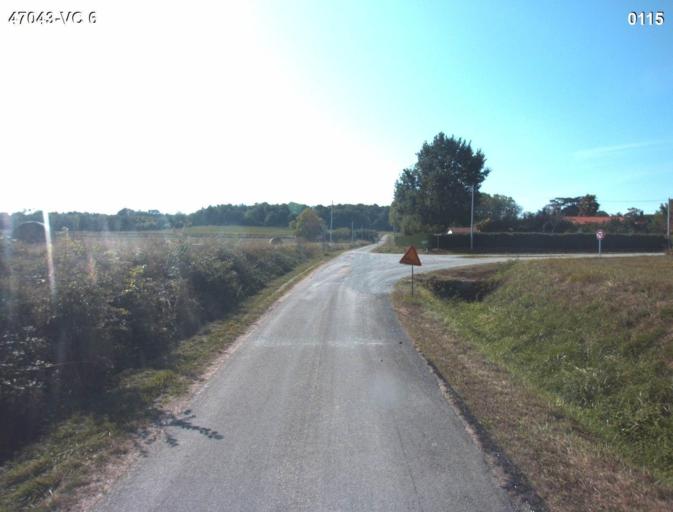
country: FR
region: Aquitaine
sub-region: Departement du Lot-et-Garonne
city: Buzet-sur-Baise
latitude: 44.2394
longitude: 0.3165
